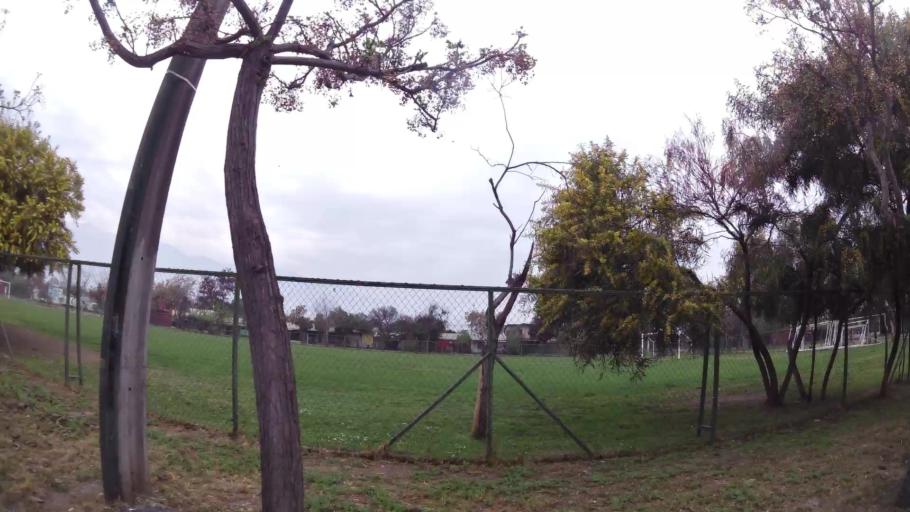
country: CL
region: Santiago Metropolitan
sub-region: Provincia de Santiago
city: Villa Presidente Frei, Nunoa, Santiago, Chile
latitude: -33.4710
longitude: -70.5935
